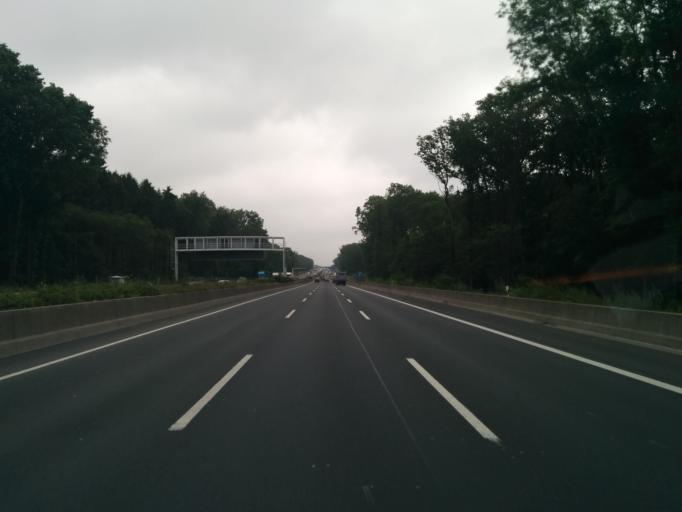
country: DE
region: North Rhine-Westphalia
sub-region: Regierungsbezirk Arnsberg
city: Bonen
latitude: 51.6035
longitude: 7.7209
